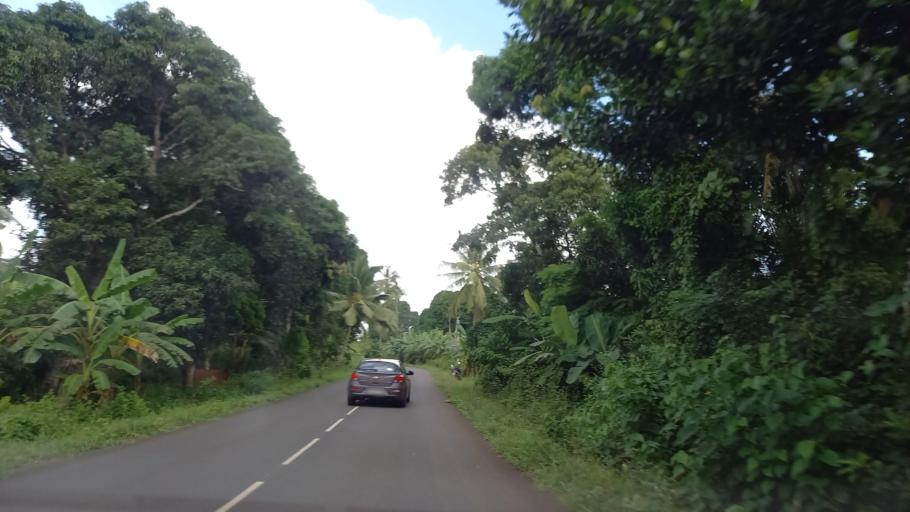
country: YT
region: Boueni
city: Boueni
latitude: -12.9179
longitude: 45.1017
